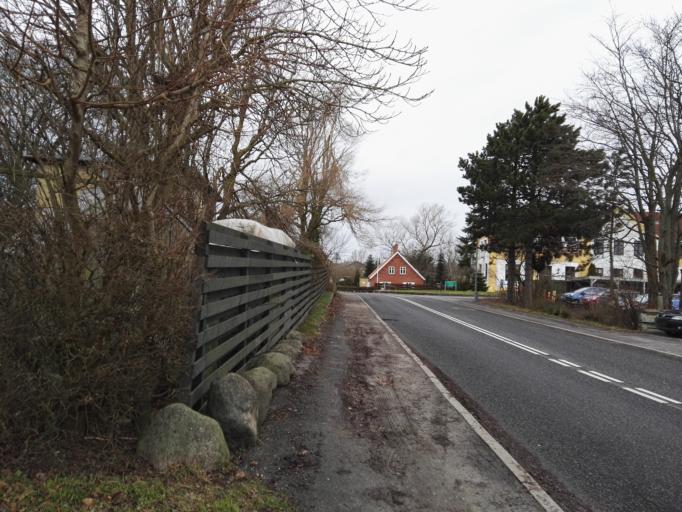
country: DK
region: Zealand
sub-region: Lejre Kommune
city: Ejby
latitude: 55.6847
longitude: 11.9199
